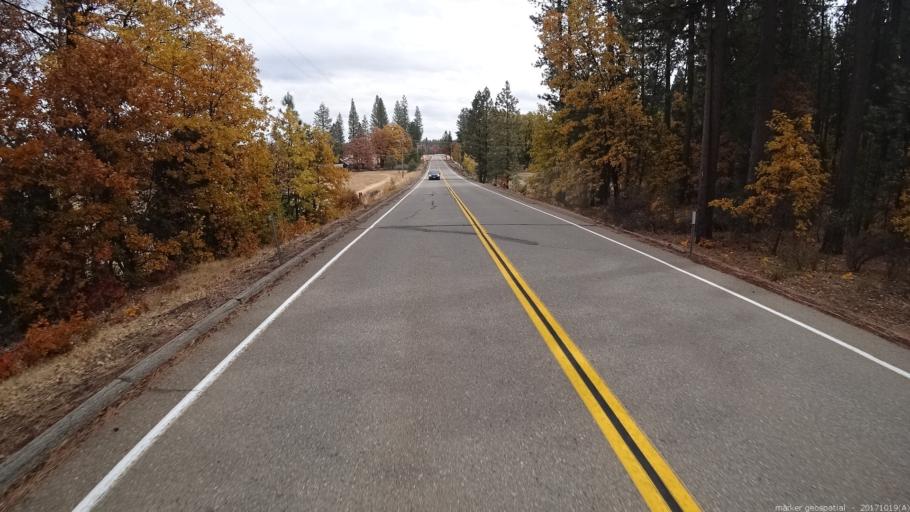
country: US
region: California
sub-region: Shasta County
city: Burney
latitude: 41.0969
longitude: -121.5554
